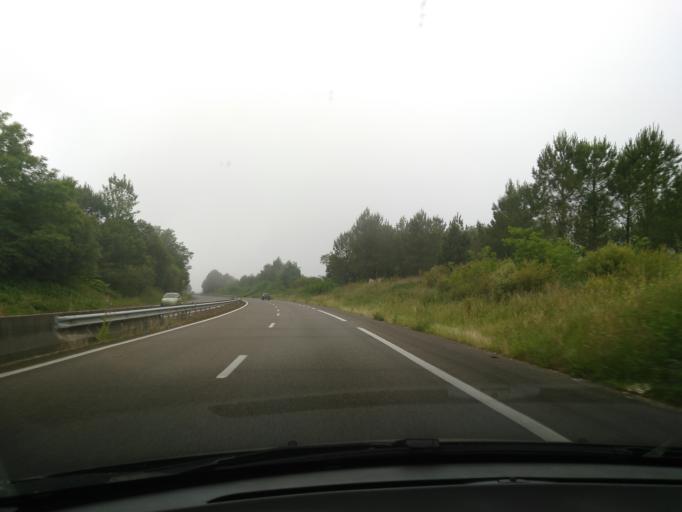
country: FR
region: Aquitaine
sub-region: Departement des Landes
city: Meilhan
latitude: 43.8626
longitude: -0.6920
